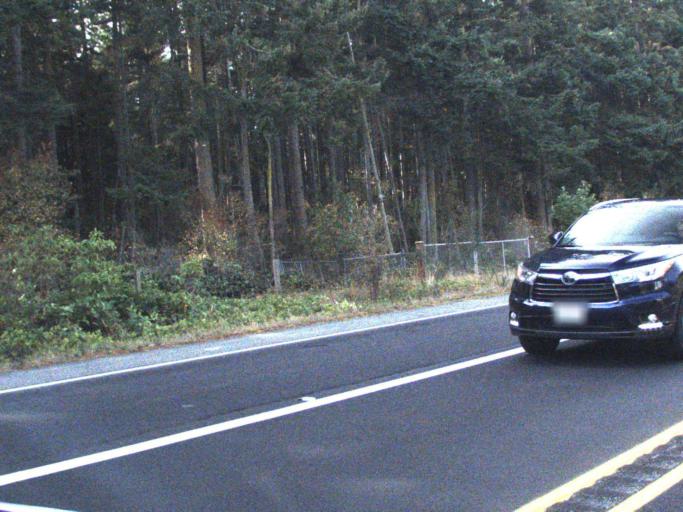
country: US
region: Washington
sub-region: Island County
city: Coupeville
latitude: 48.2111
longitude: -122.7254
